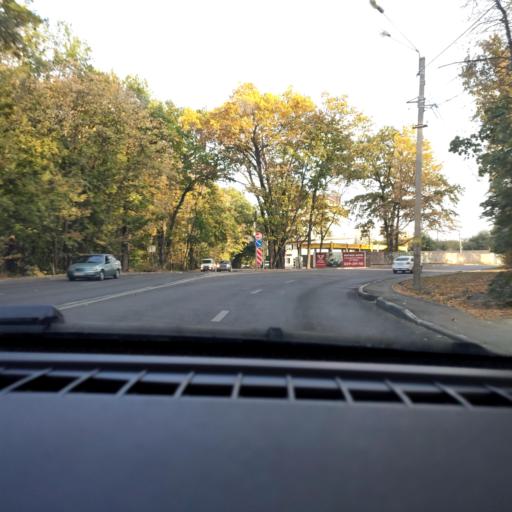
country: RU
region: Voronezj
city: Voronezh
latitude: 51.7257
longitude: 39.2151
